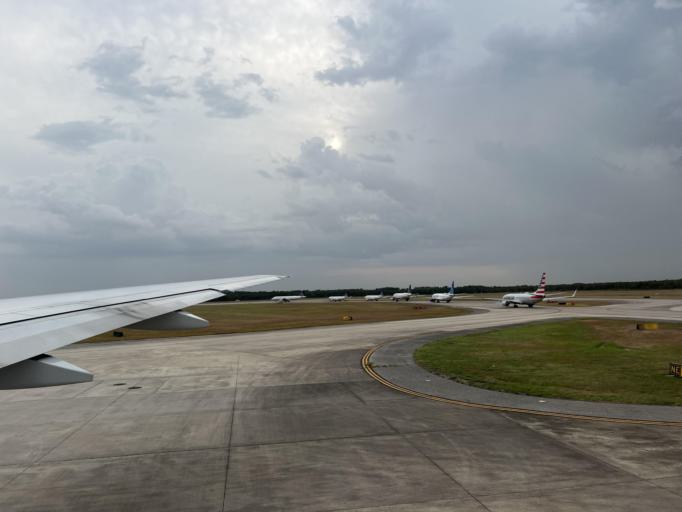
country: US
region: Texas
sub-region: Harris County
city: Aldine
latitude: 29.9900
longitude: -95.3549
